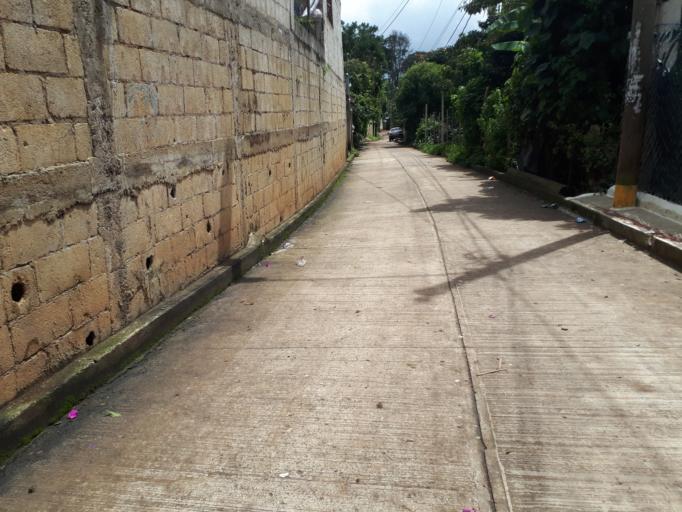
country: GT
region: Guatemala
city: Villa Canales
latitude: 14.4594
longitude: -90.5109
